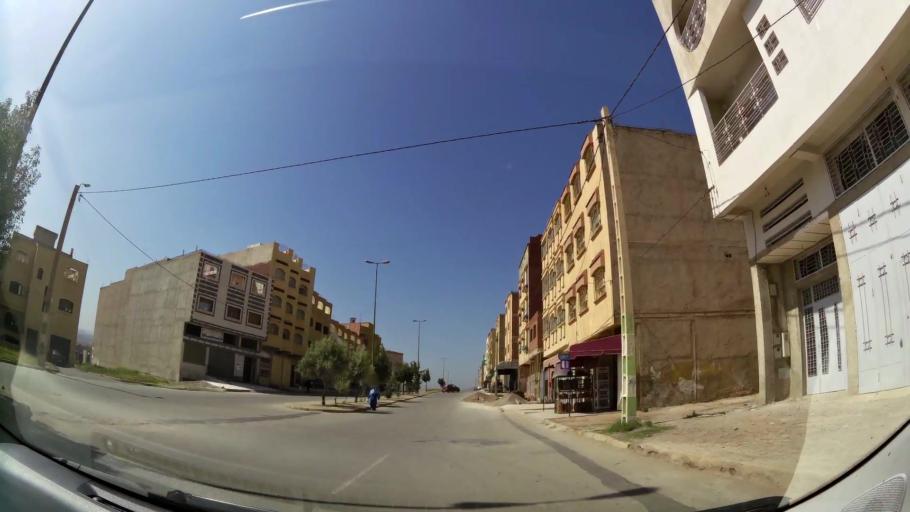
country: MA
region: Oriental
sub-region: Oujda-Angad
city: Oujda
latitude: 34.6763
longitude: -1.9380
